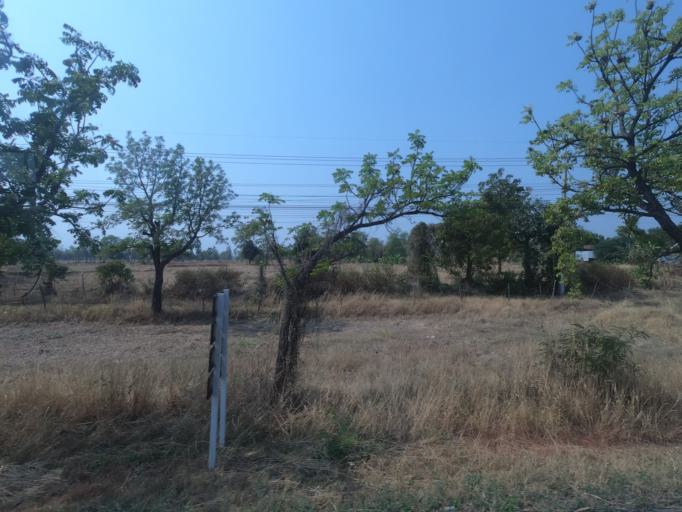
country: TH
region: Nakhon Ratchasima
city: Non Daeng
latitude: 15.3738
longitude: 102.4589
